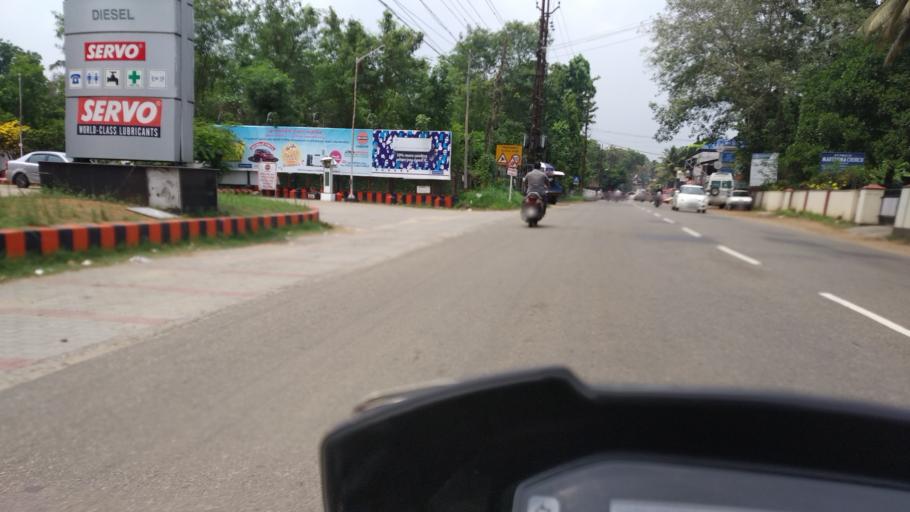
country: IN
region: Kerala
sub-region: Ernakulam
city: Perumpavur
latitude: 10.1167
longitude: 76.4872
